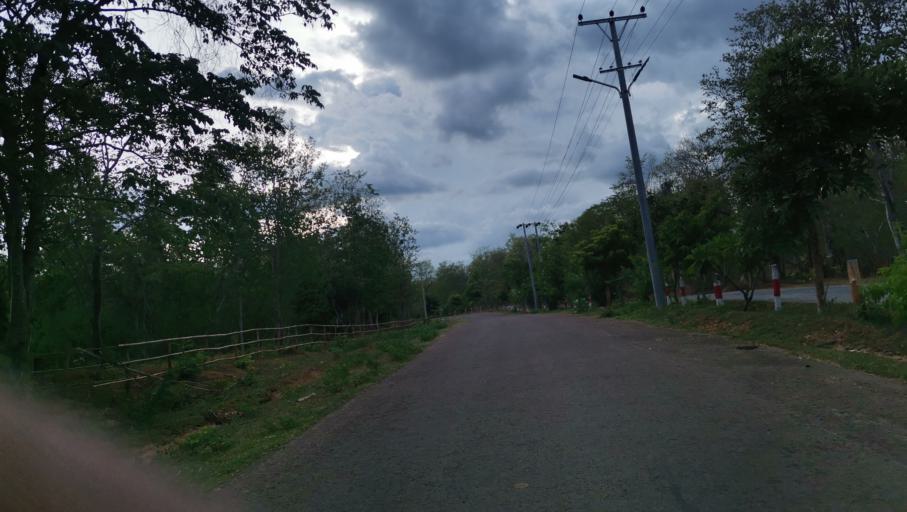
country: MM
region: Magway
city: Minbu
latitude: 20.0882
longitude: 94.5710
